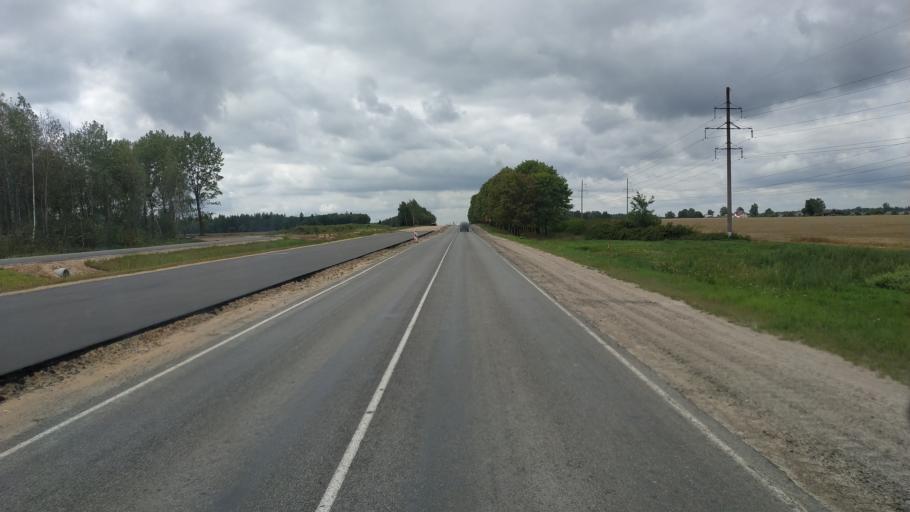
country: BY
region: Mogilev
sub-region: Mahilyowski Rayon
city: Kadino
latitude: 53.8692
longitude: 30.4664
